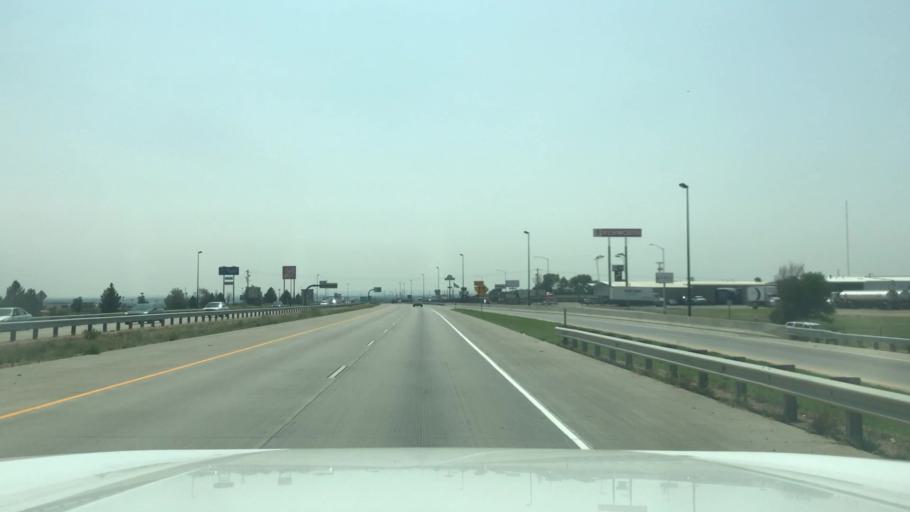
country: US
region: Colorado
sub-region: Pueblo County
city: Pueblo
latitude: 38.3190
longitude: -104.6156
